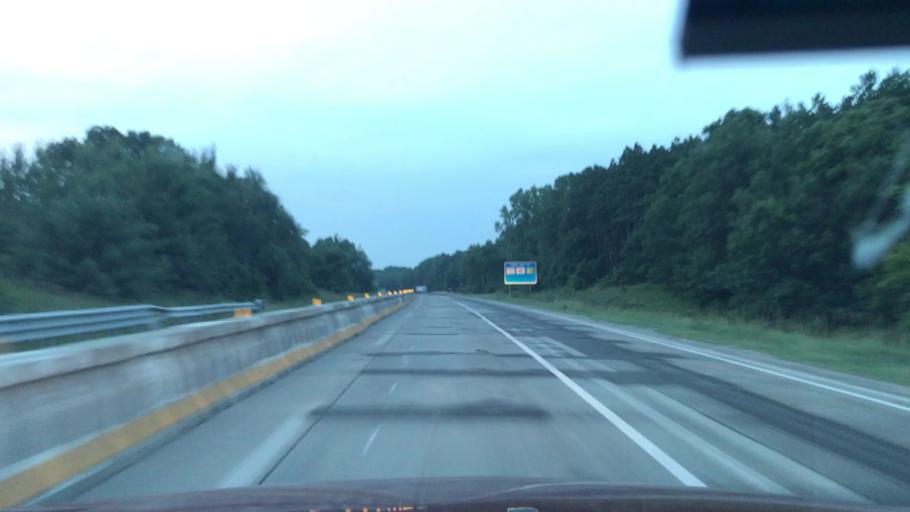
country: US
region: Michigan
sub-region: Kent County
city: Rockford
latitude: 43.1620
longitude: -85.5765
